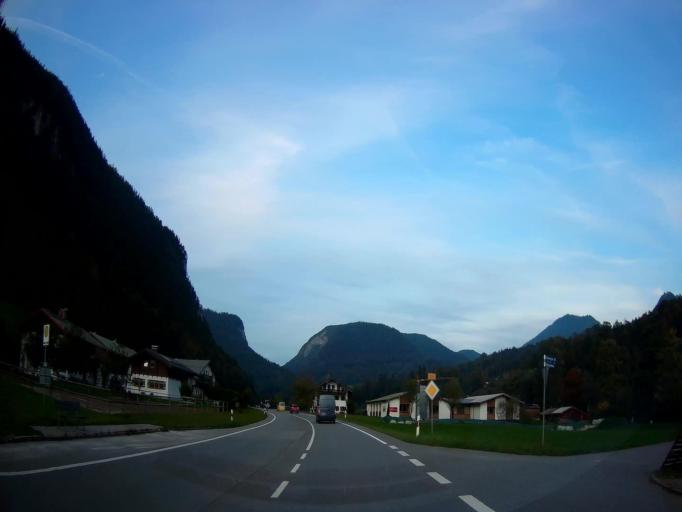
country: DE
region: Bavaria
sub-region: Upper Bavaria
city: Berchtesgaden
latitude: 47.6452
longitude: 13.0287
